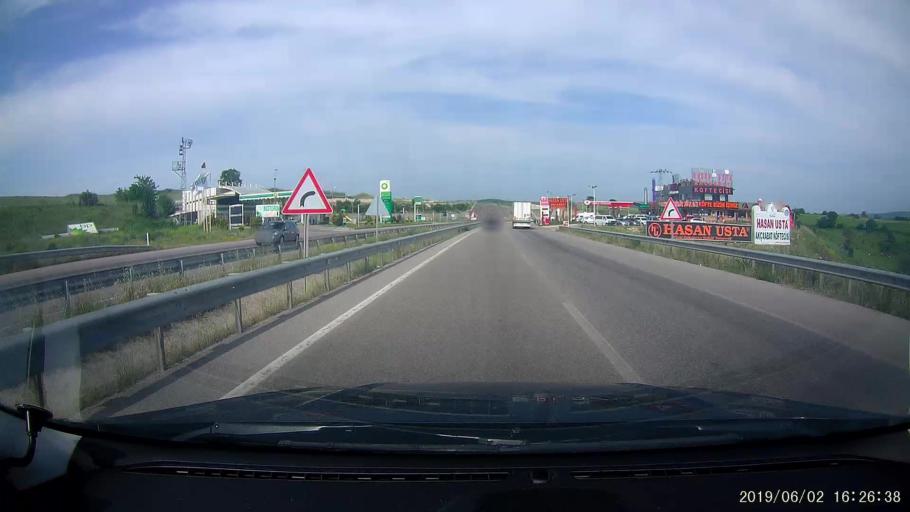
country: TR
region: Samsun
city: Ladik
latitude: 41.0008
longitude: 35.8076
